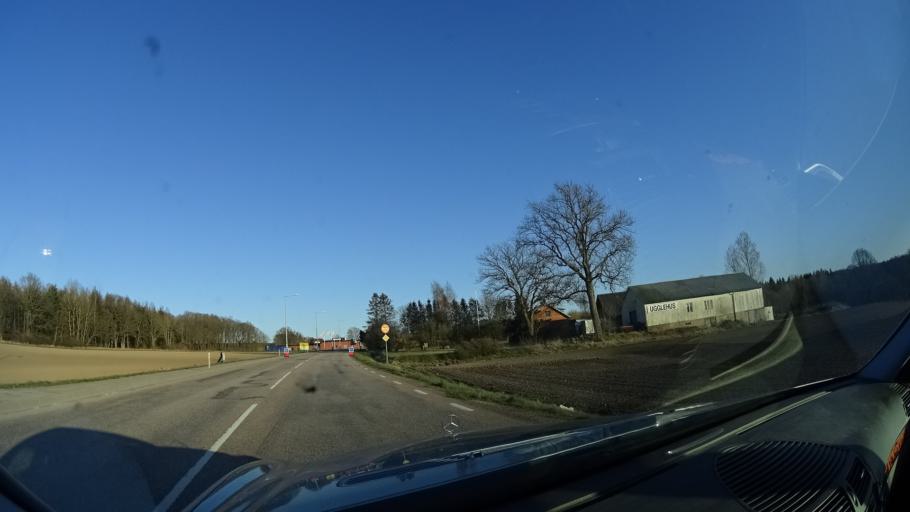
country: SE
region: Skane
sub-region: Bjuvs Kommun
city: Billesholm
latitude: 56.0591
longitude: 12.9906
